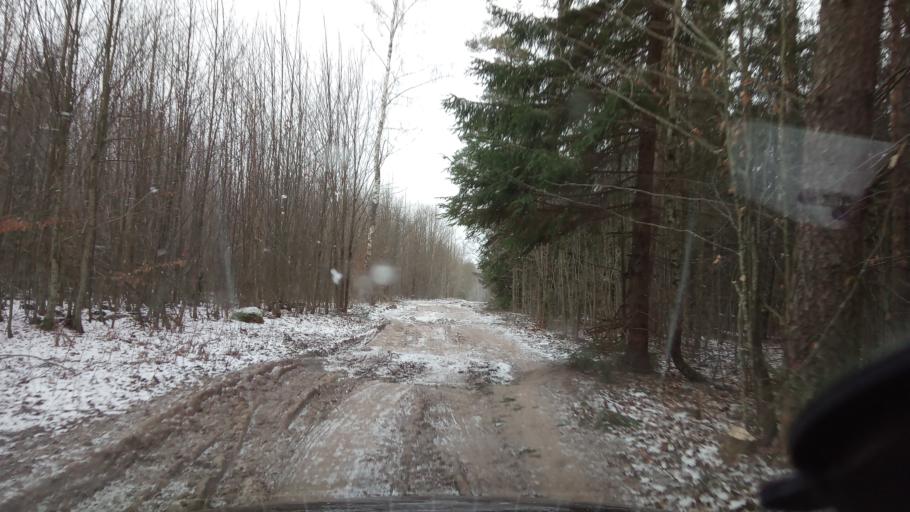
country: LT
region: Alytaus apskritis
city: Varena
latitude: 54.1353
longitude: 24.7003
